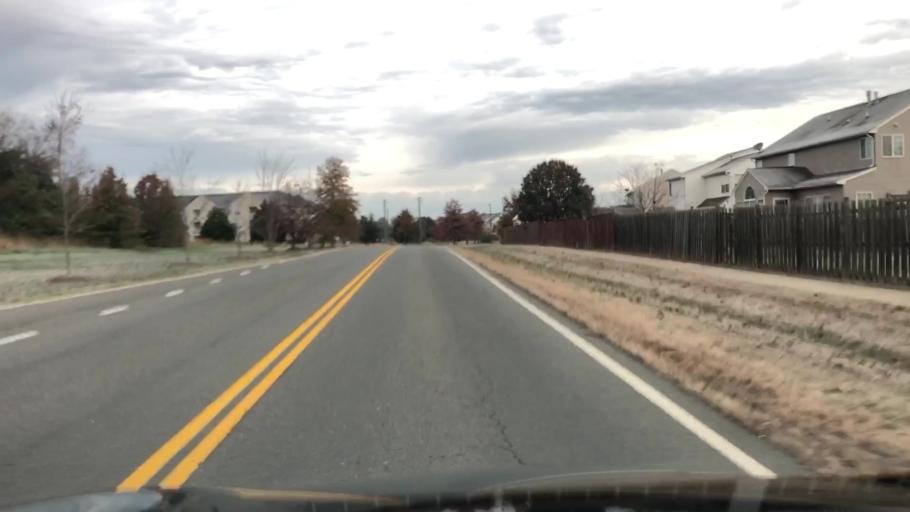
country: US
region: Virginia
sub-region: Fauquier County
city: Bealeton
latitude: 38.5802
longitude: -77.7604
